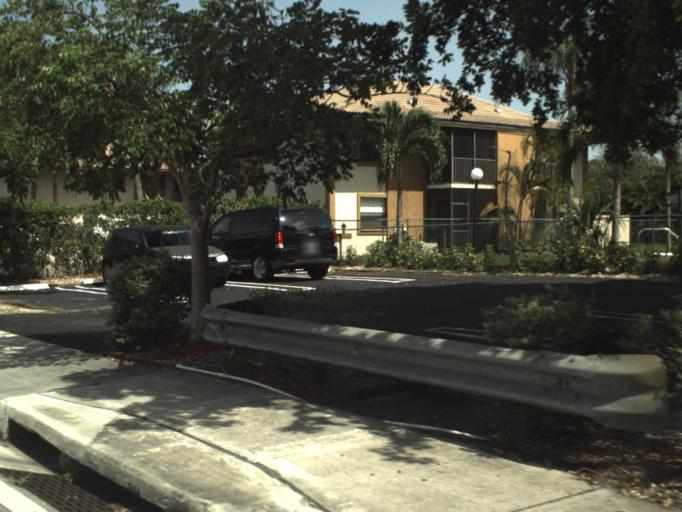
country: US
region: Florida
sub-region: Broward County
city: Coral Springs
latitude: 26.2726
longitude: -80.2768
